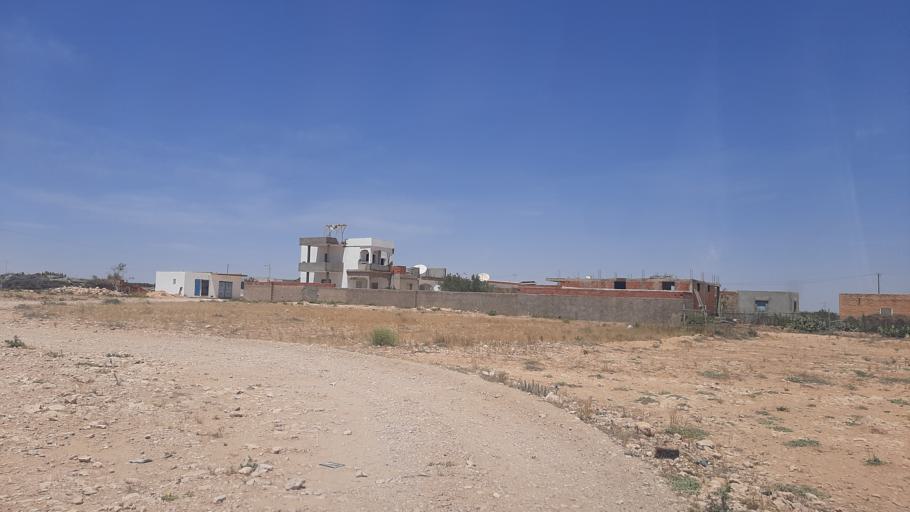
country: TN
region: Safaqis
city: Bi'r `Ali Bin Khalifah
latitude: 34.5682
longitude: 10.3471
